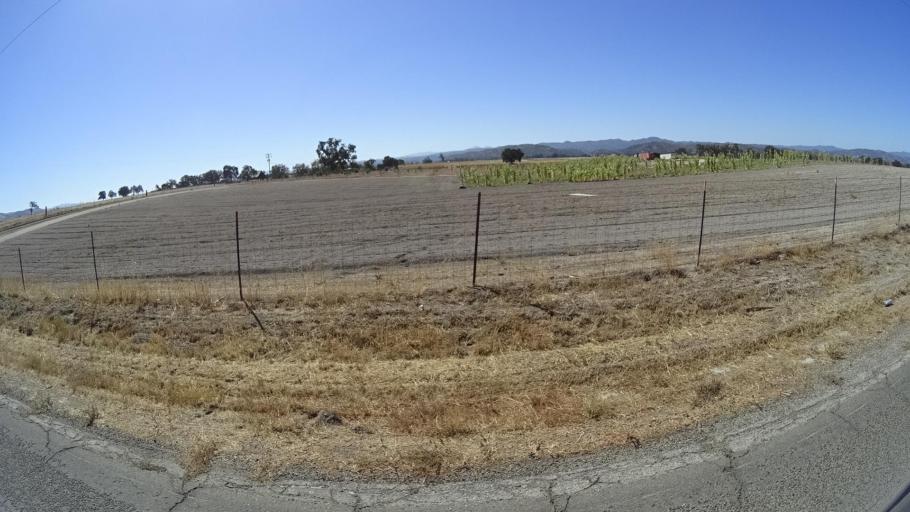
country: US
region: California
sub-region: Monterey County
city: King City
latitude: 35.9443
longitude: -121.0740
